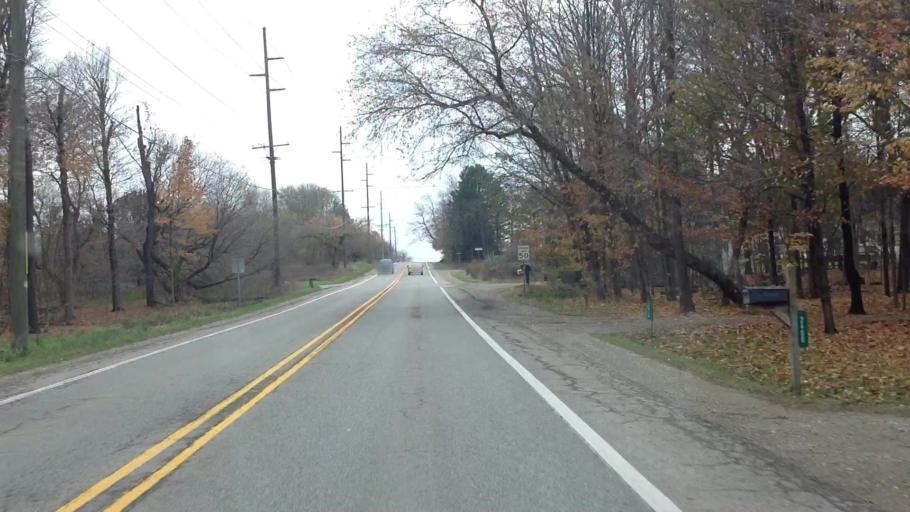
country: US
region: Michigan
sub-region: Oakland County
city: Milford
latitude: 42.6150
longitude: -83.6606
